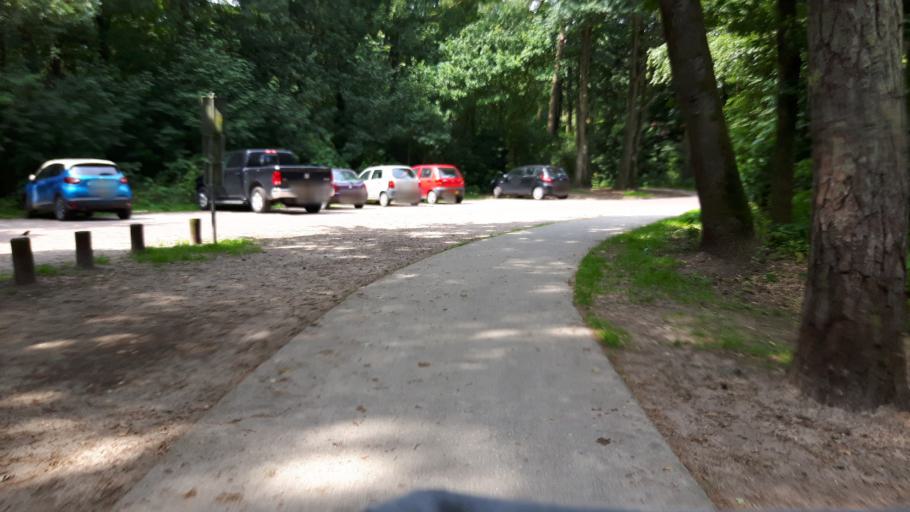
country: NL
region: Utrecht
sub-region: Gemeente Soest
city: Soest
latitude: 52.1554
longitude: 5.3005
